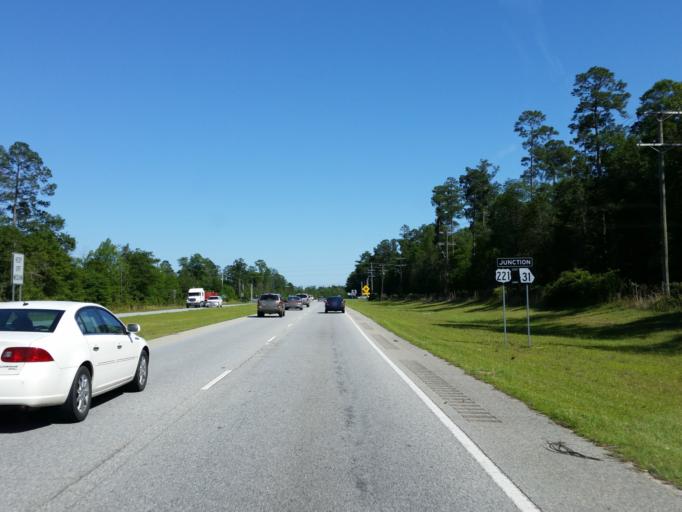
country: US
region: Georgia
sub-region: Lowndes County
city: Valdosta
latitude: 30.8775
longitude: -83.2398
